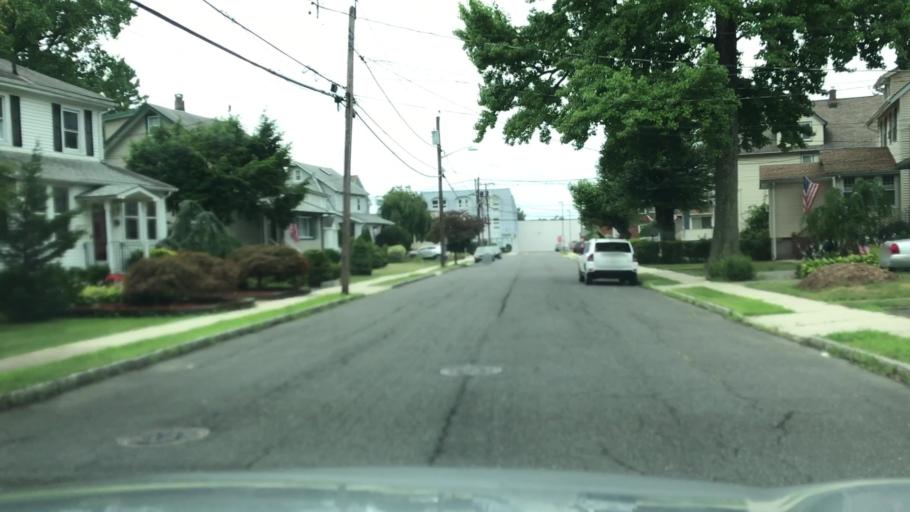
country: US
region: New Jersey
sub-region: Bergen County
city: Dumont
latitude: 40.9374
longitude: -73.9929
